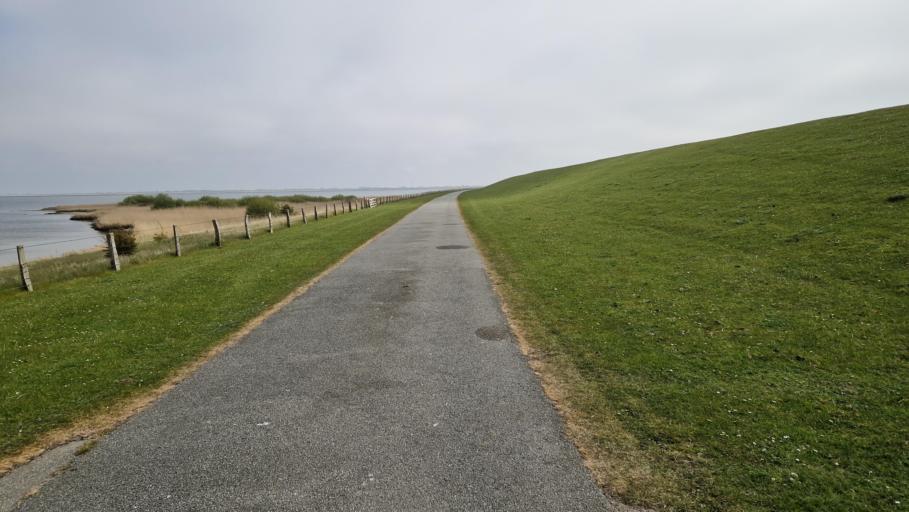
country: DE
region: Schleswig-Holstein
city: Elisabeth-Sophien-Koog
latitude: 54.5514
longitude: 8.8775
